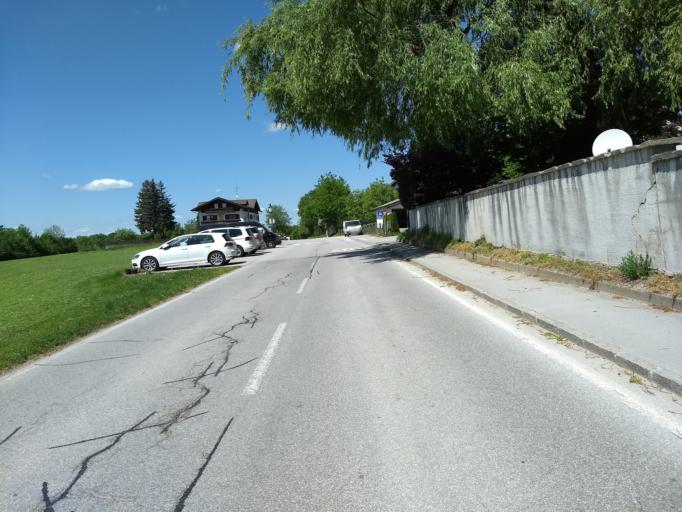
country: AT
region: Salzburg
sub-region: Politischer Bezirk Salzburg-Umgebung
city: Bergheim
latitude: 47.8360
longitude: 13.0272
